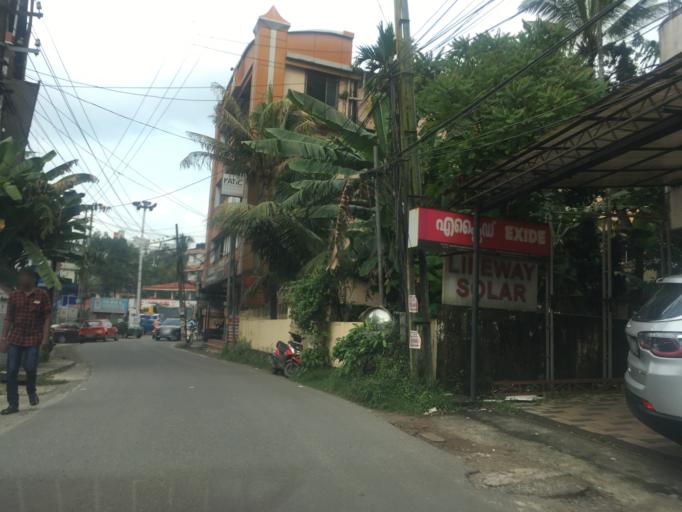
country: IN
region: Kerala
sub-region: Ernakulam
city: Elur
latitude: 10.0254
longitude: 76.3126
